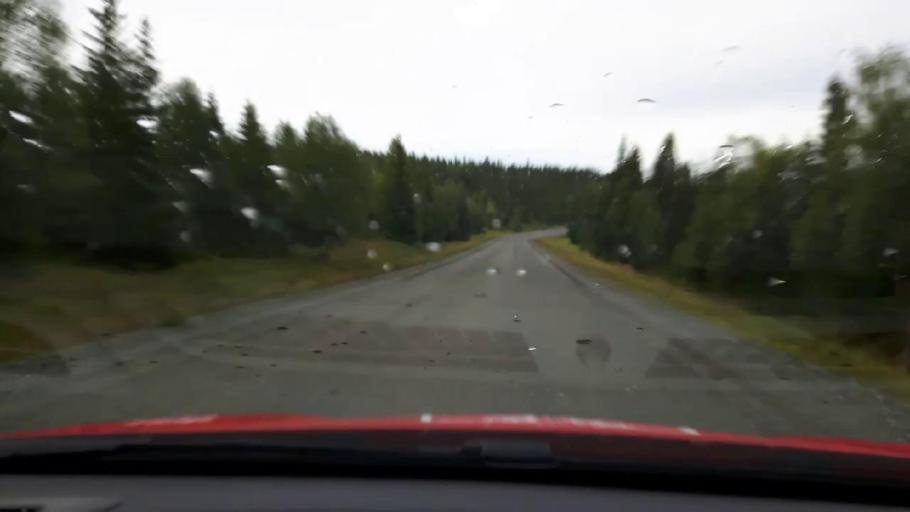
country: SE
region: Jaemtland
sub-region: Are Kommun
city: Are
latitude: 63.4154
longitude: 12.7611
